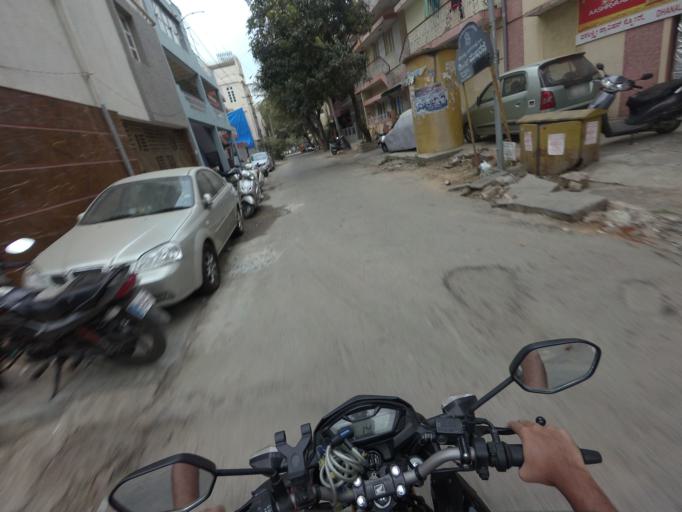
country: IN
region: Karnataka
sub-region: Bangalore Urban
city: Bangalore
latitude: 12.9679
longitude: 77.5439
